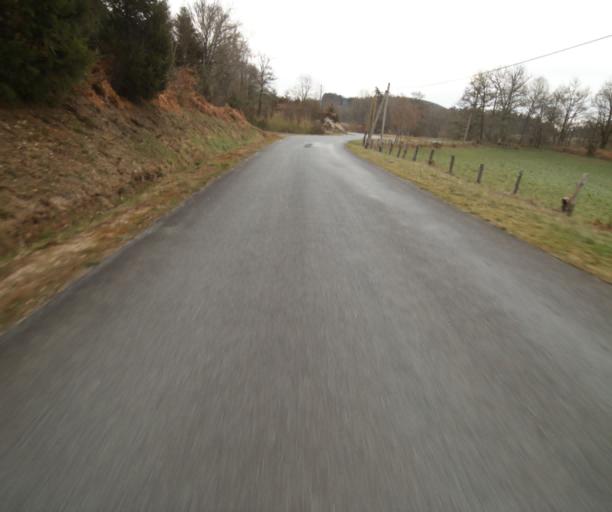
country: FR
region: Limousin
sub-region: Departement de la Correze
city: Correze
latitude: 45.4236
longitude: 1.8569
